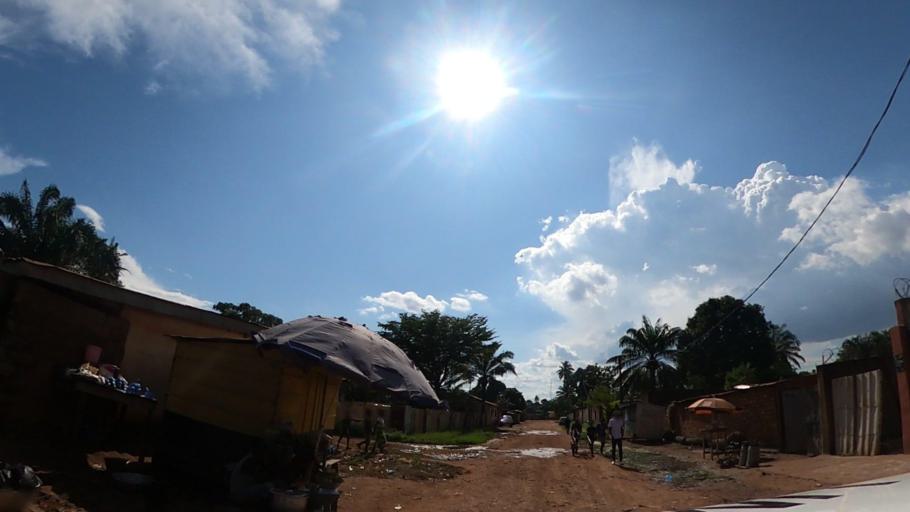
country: CF
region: Bangui
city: Bangui
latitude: 4.3761
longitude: 18.5523
